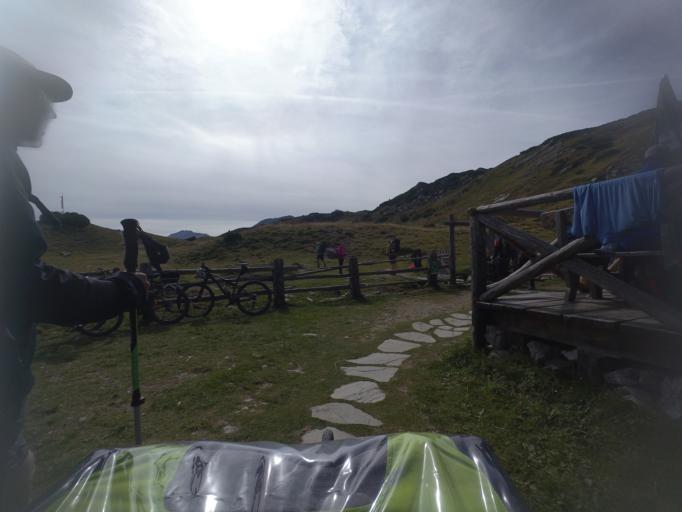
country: AT
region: Salzburg
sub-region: Politischer Bezirk Tamsweg
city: Tweng
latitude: 47.2806
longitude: 13.6000
